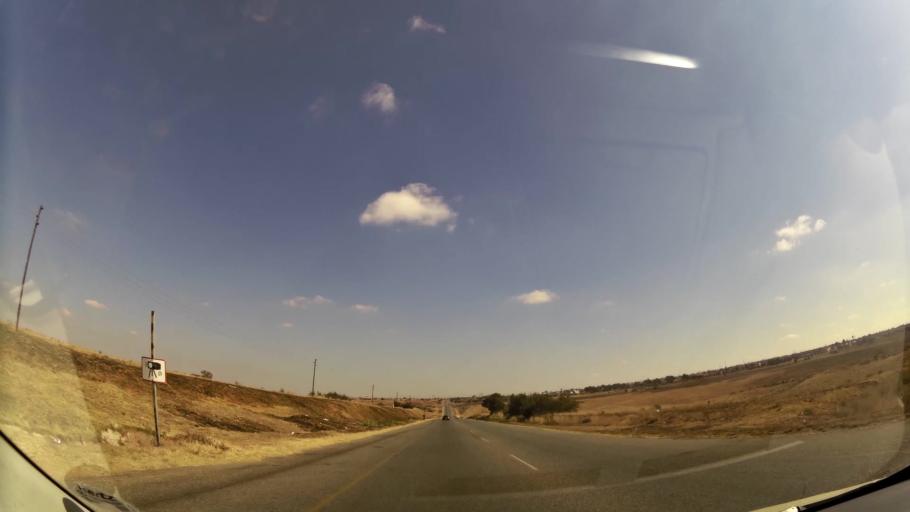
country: ZA
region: Gauteng
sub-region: West Rand District Municipality
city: Randfontein
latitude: -26.1762
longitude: 27.7711
